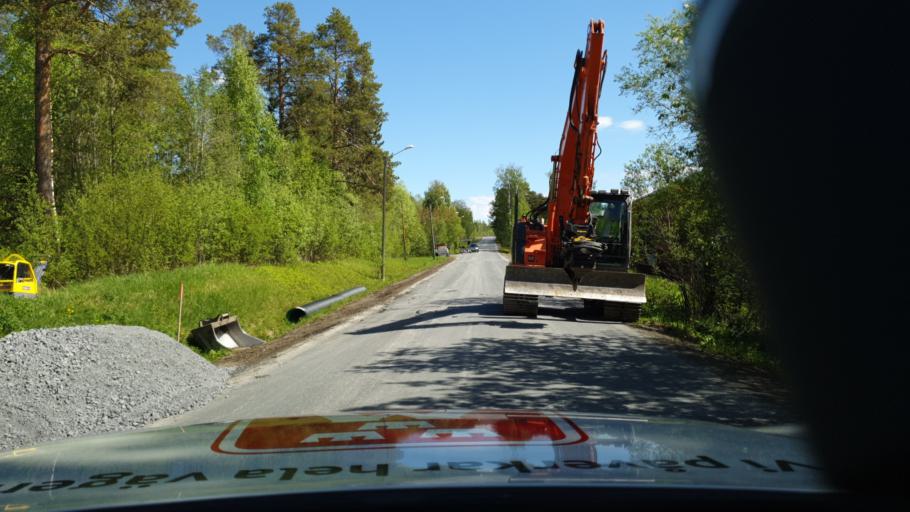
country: SE
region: Jaemtland
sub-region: Krokoms Kommun
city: Valla
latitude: 63.3025
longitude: 13.8349
